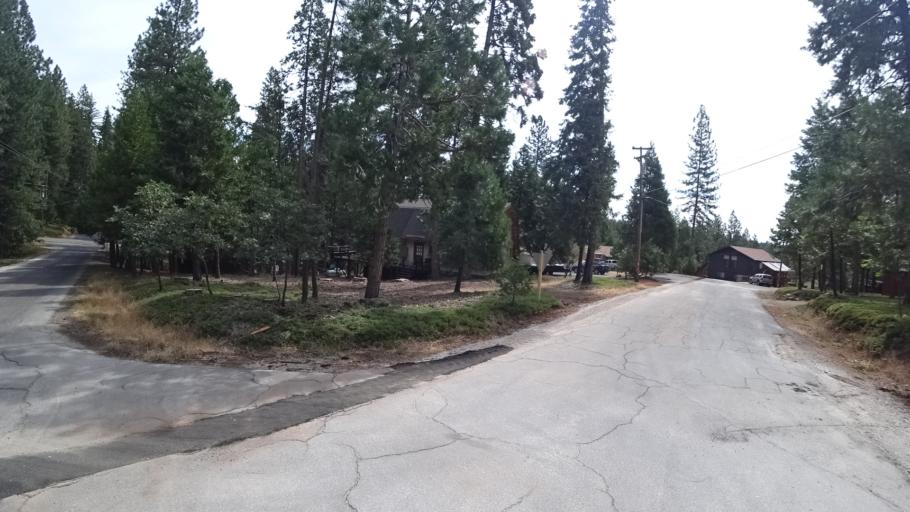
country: US
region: California
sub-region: Calaveras County
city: Arnold
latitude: 38.2481
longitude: -120.3427
